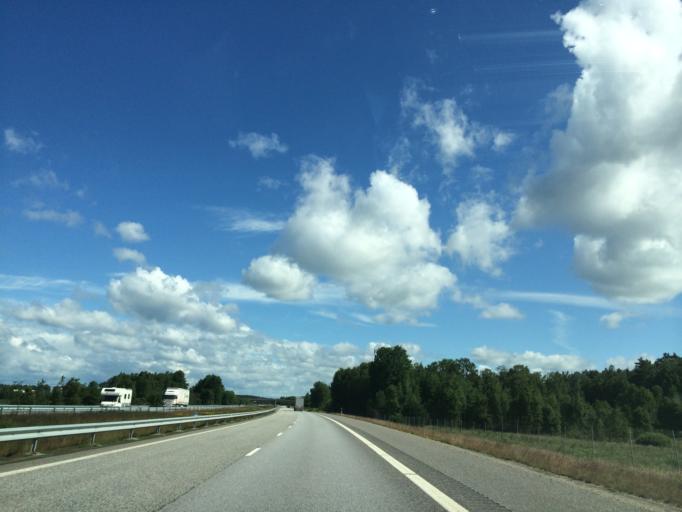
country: SE
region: Kronoberg
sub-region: Markaryds Kommun
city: Stromsnasbruk
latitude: 56.6370
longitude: 13.7977
